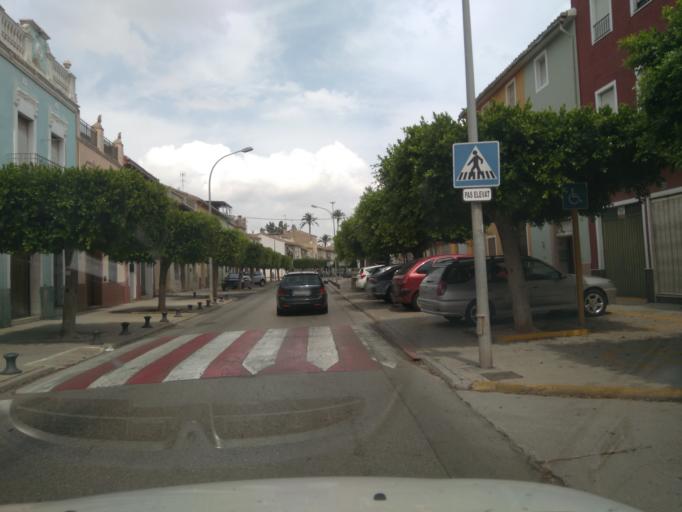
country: ES
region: Valencia
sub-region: Provincia de Valencia
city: Carcaixent
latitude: 39.1277
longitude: -0.4494
